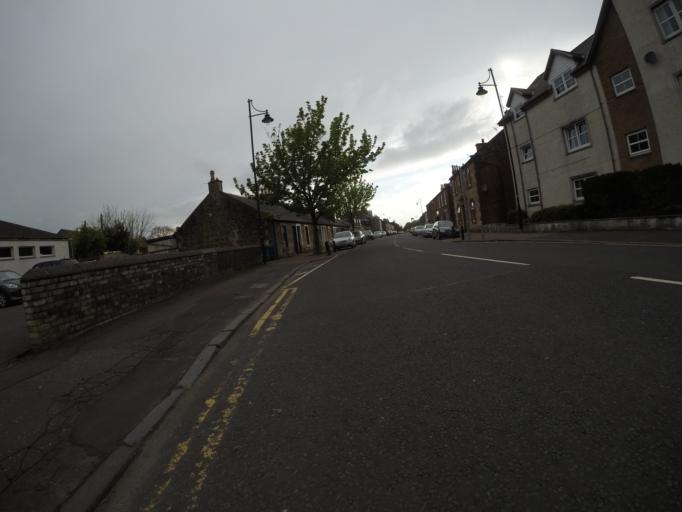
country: GB
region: Scotland
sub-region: North Ayrshire
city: Dreghorn
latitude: 55.6109
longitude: -4.6133
